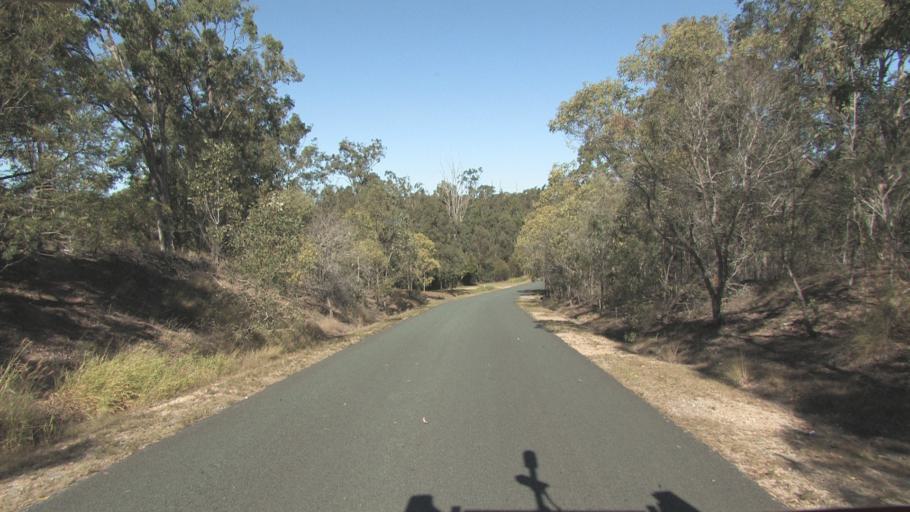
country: AU
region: Queensland
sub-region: Ipswich
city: Springfield Lakes
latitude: -27.7127
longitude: 152.9321
